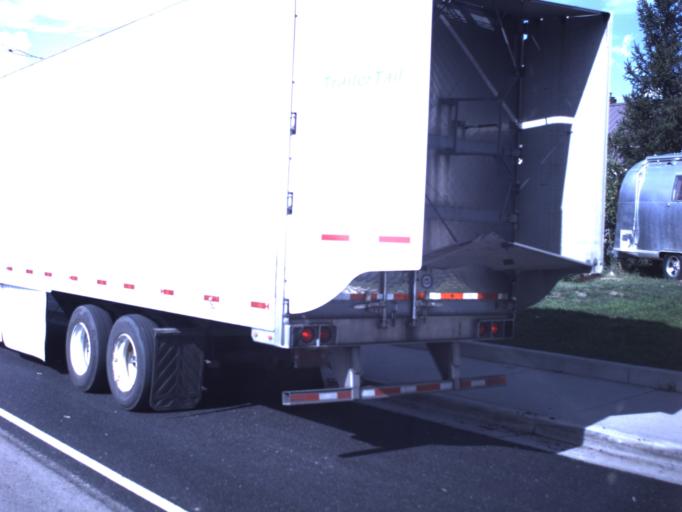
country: US
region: Utah
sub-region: Wasatch County
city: Heber
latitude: 40.4971
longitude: -111.4135
